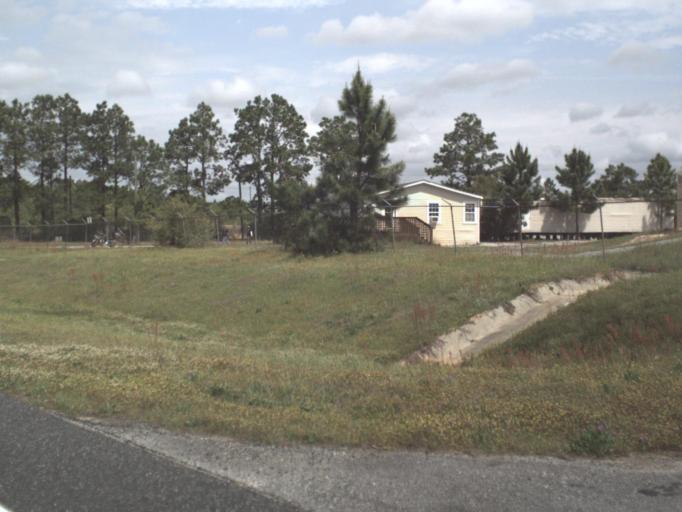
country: US
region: Florida
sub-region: Santa Rosa County
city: East Milton
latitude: 30.5943
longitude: -86.9399
